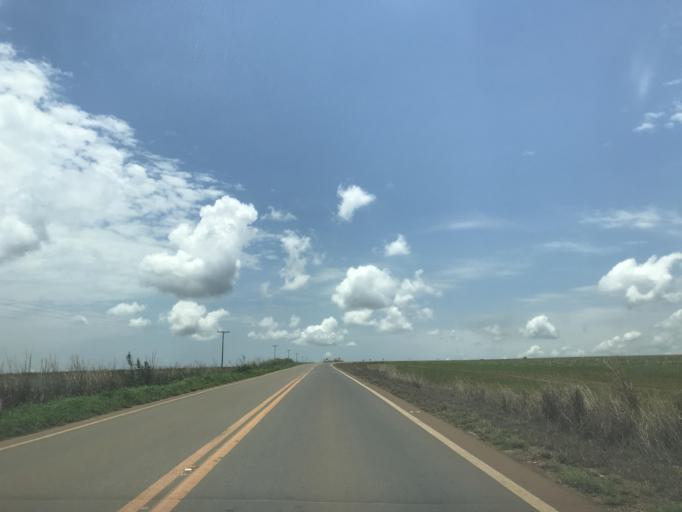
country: BR
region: Goias
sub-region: Luziania
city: Luziania
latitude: -16.4899
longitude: -48.2014
